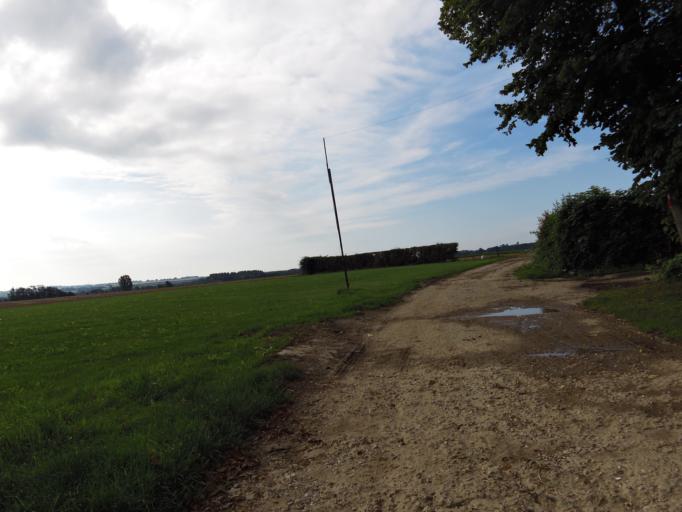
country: NL
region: Limburg
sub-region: Gemeente Nuth
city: Nuth
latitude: 50.8953
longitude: 5.8934
